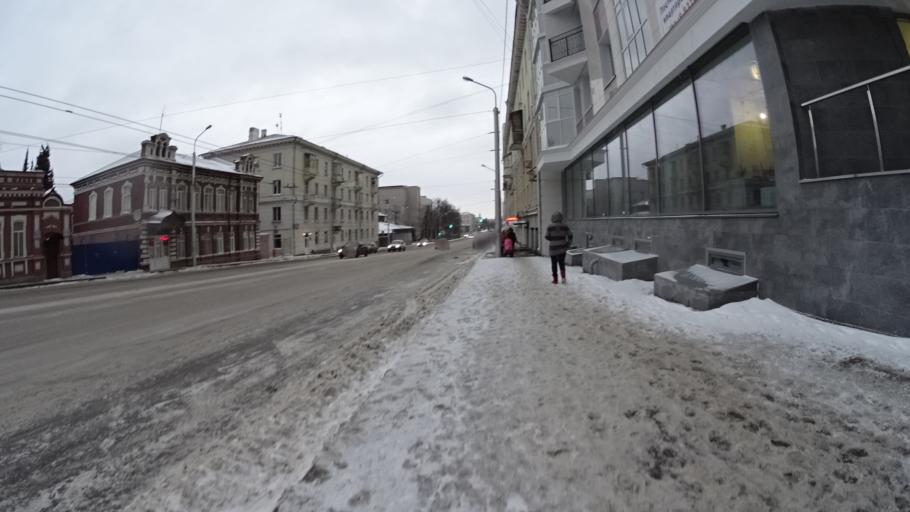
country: RU
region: Bashkortostan
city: Ufa
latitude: 54.7333
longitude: 55.9446
